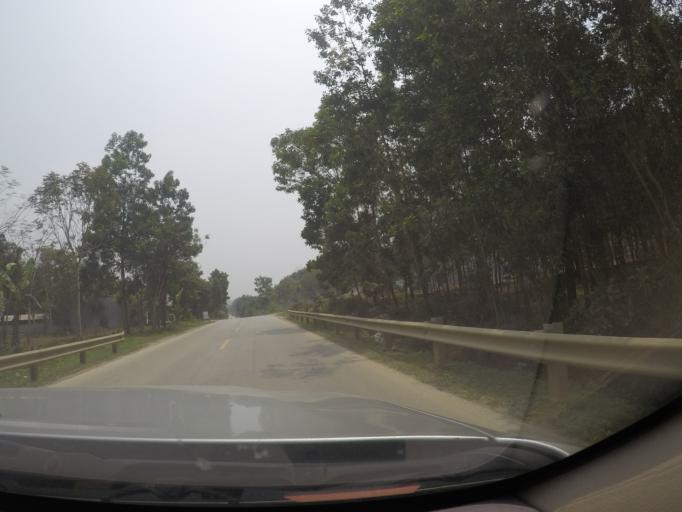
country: VN
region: Thanh Hoa
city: Thi Tran Thuong Xuan
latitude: 19.8202
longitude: 105.3915
